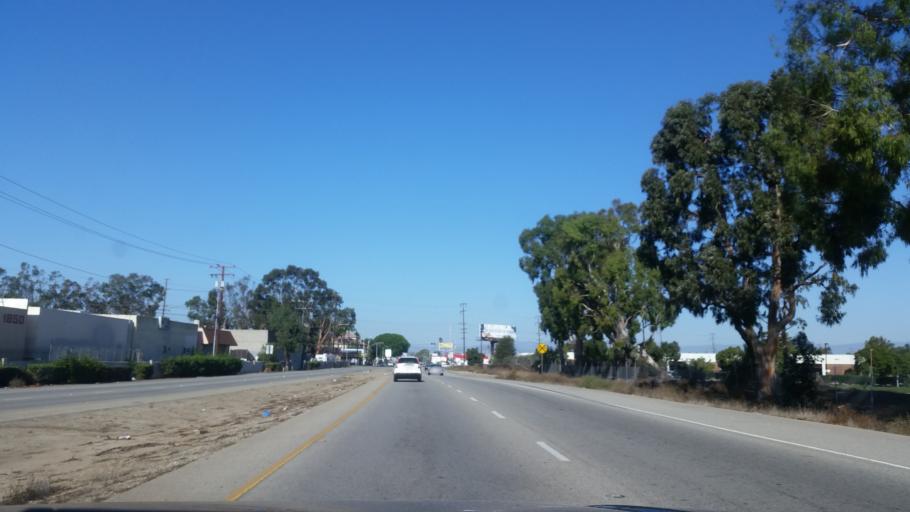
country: US
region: California
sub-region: Ventura County
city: Oxnard
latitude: 34.1812
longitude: -119.1666
